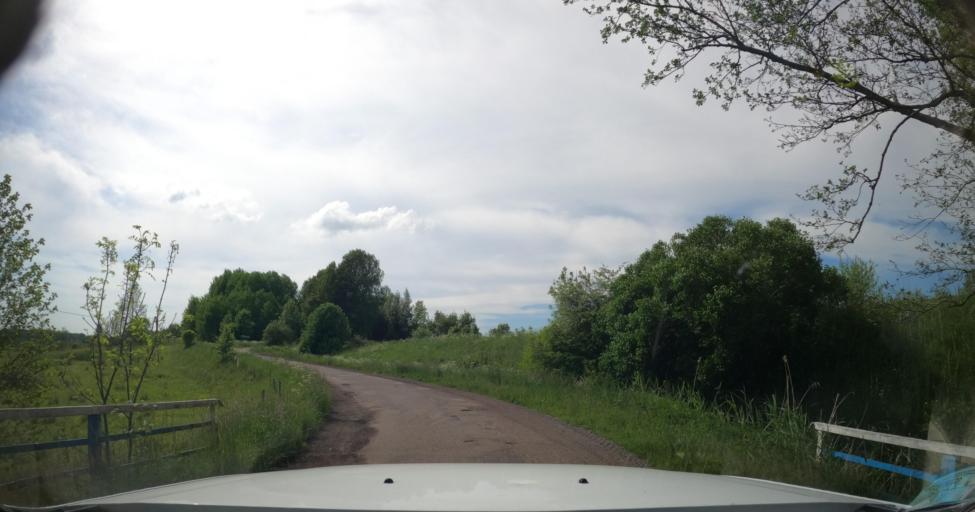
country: PL
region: Warmian-Masurian Voivodeship
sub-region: Powiat lidzbarski
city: Lidzbark Warminski
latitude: 54.1126
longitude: 20.4844
